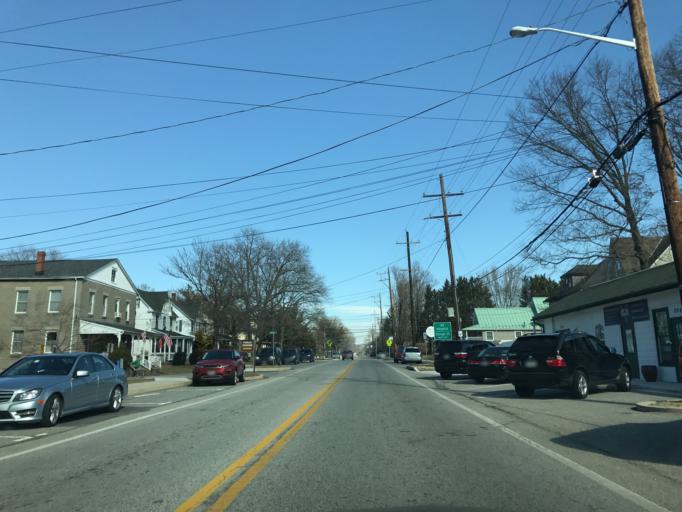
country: US
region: Maryland
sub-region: Cecil County
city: Perryville
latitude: 39.5604
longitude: -76.0714
